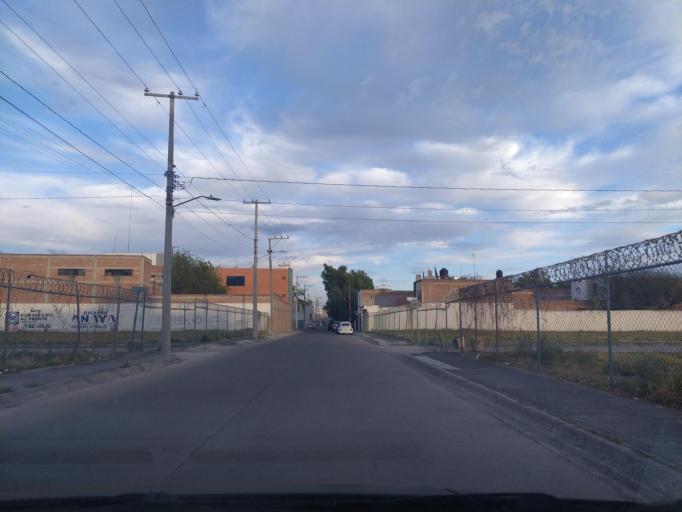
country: LA
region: Oudomxai
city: Muang La
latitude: 21.0188
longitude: 101.8676
